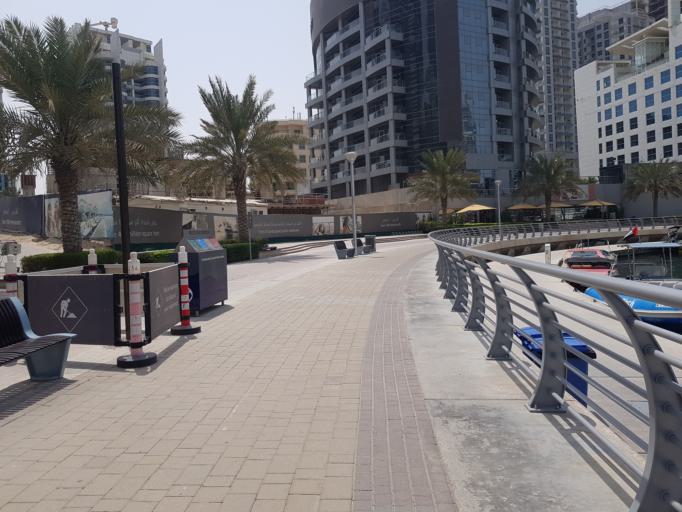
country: AE
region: Dubai
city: Dubai
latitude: 25.0692
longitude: 55.1318
